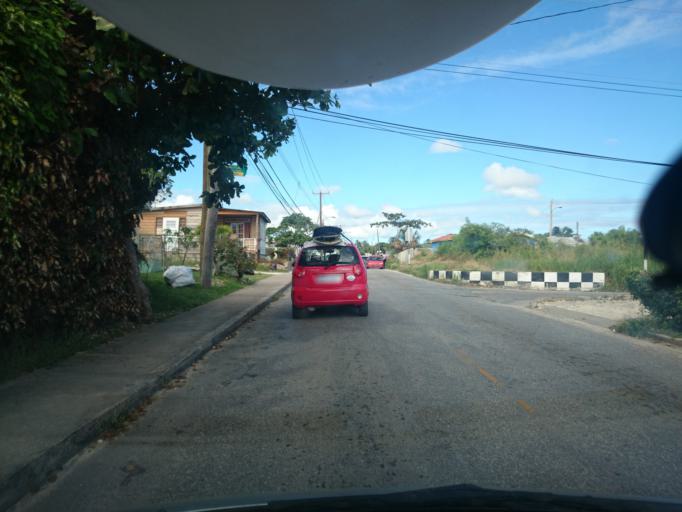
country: BB
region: Christ Church
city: Oistins
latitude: 13.0711
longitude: -59.5399
